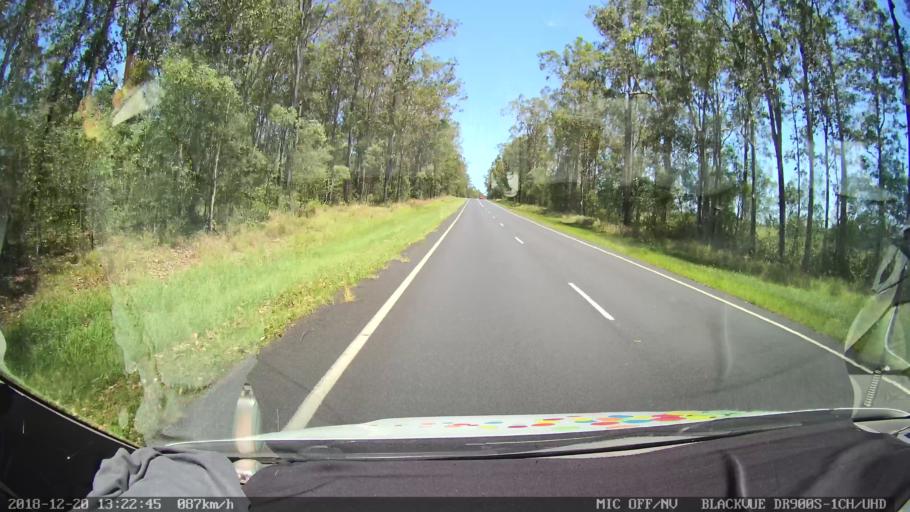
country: AU
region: New South Wales
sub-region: Richmond Valley
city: Casino
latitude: -29.0956
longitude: 153.0012
